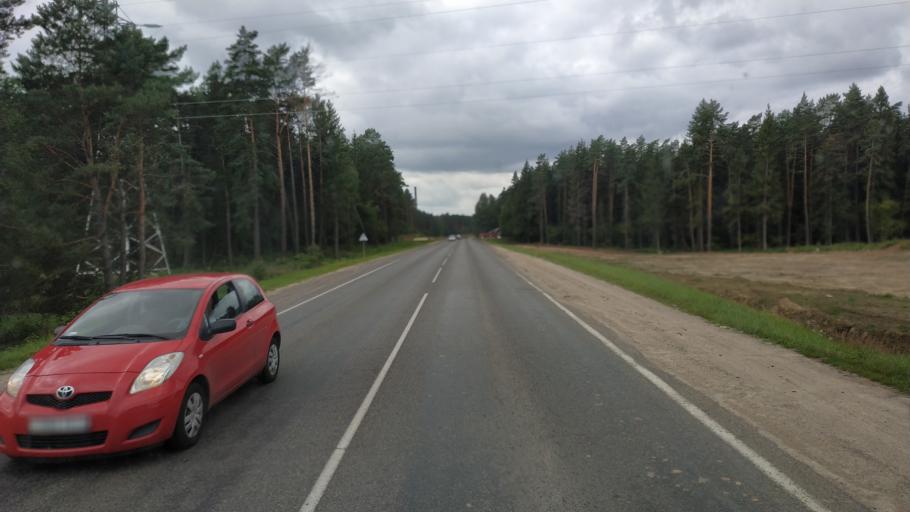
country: BY
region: Mogilev
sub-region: Mahilyowski Rayon
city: Veyno
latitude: 53.8762
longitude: 30.4262
